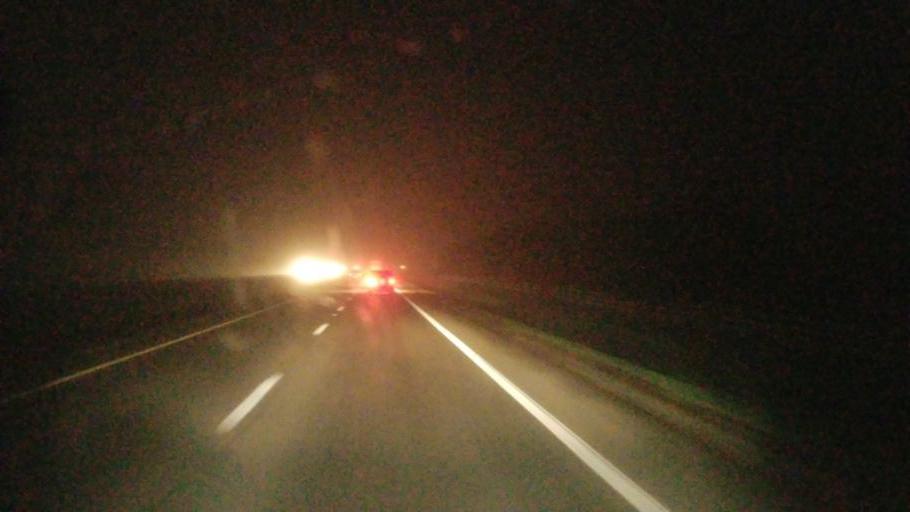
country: US
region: Ohio
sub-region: Pickaway County
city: South Bloomfield
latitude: 39.7118
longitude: -82.9873
